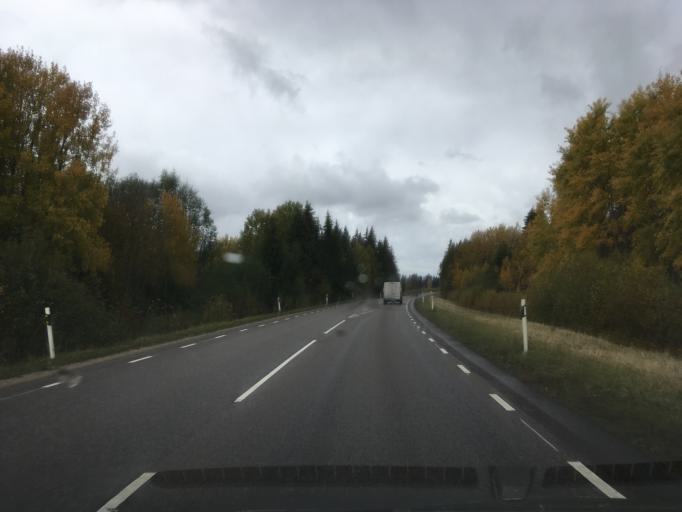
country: EE
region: Harju
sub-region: Anija vald
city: Kehra
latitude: 59.3336
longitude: 25.3128
